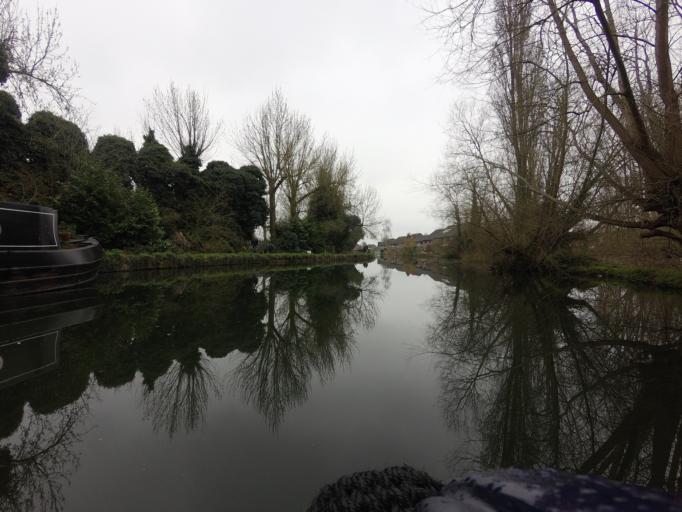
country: GB
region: England
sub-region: Hertfordshire
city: Kings Langley
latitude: 51.7176
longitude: -0.4463
